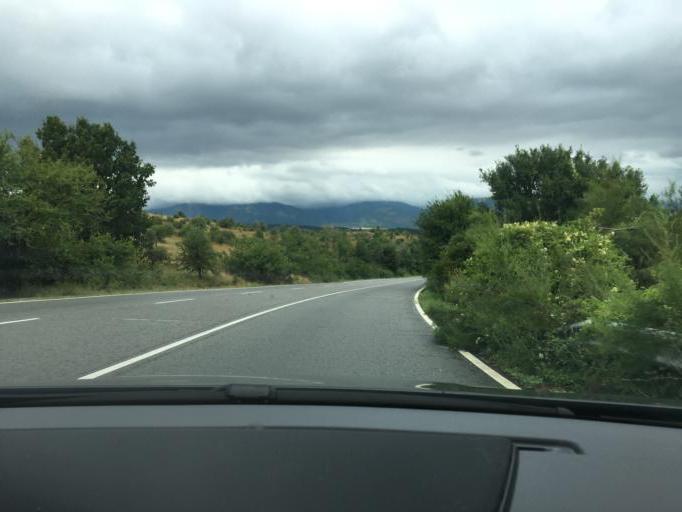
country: BG
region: Kyustendil
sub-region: Obshtina Bobovdol
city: Bobovdol
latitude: 42.2693
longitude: 22.9439
